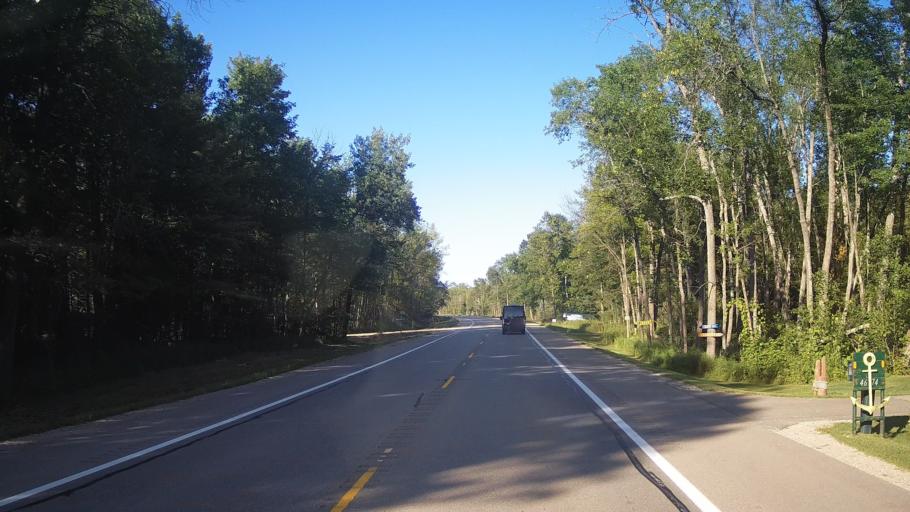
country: US
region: Michigan
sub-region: Menominee County
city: Menominee
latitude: 45.2803
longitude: -87.4584
